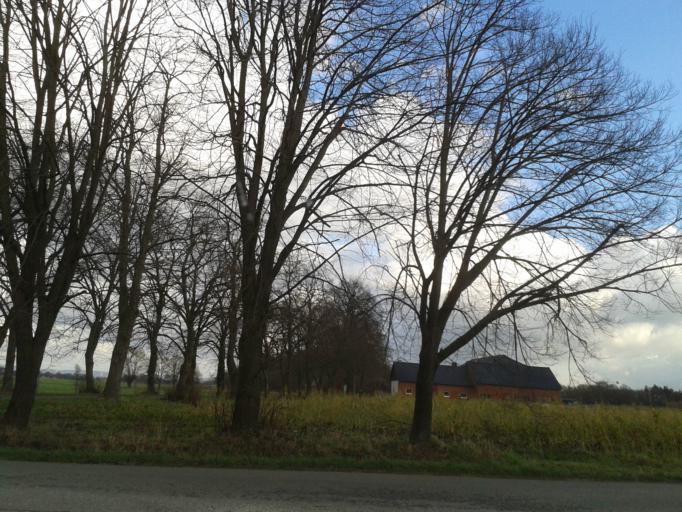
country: DE
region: North Rhine-Westphalia
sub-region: Regierungsbezirk Detmold
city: Salzkotten
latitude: 51.7272
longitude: 8.6341
